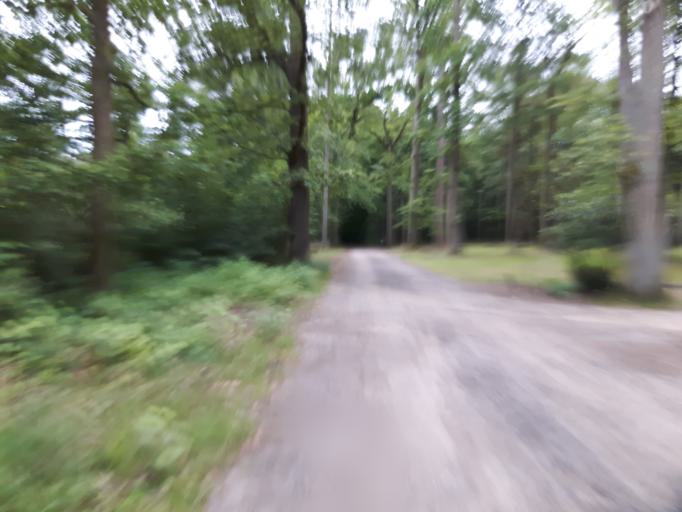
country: DE
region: Lower Saxony
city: Vierhofen
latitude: 53.2622
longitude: 10.1854
